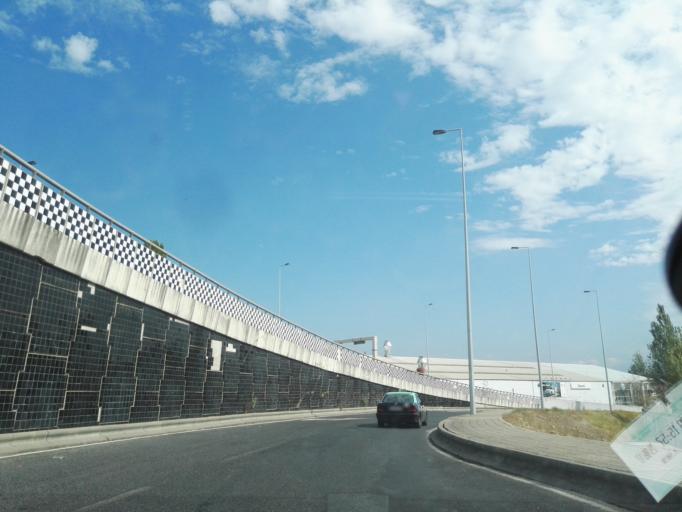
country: PT
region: Lisbon
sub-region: Loures
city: Moscavide
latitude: 38.7536
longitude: -9.0962
